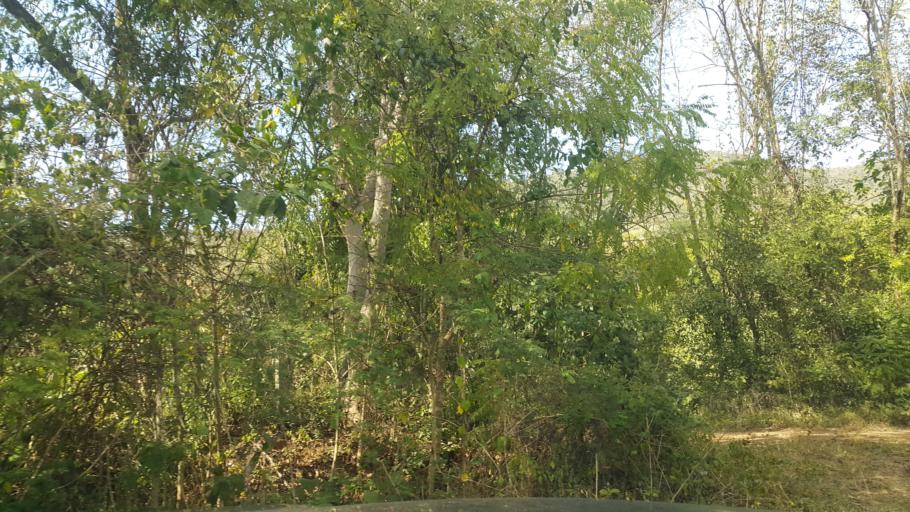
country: TH
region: Chiang Mai
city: Mae On
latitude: 18.7470
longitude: 99.2054
